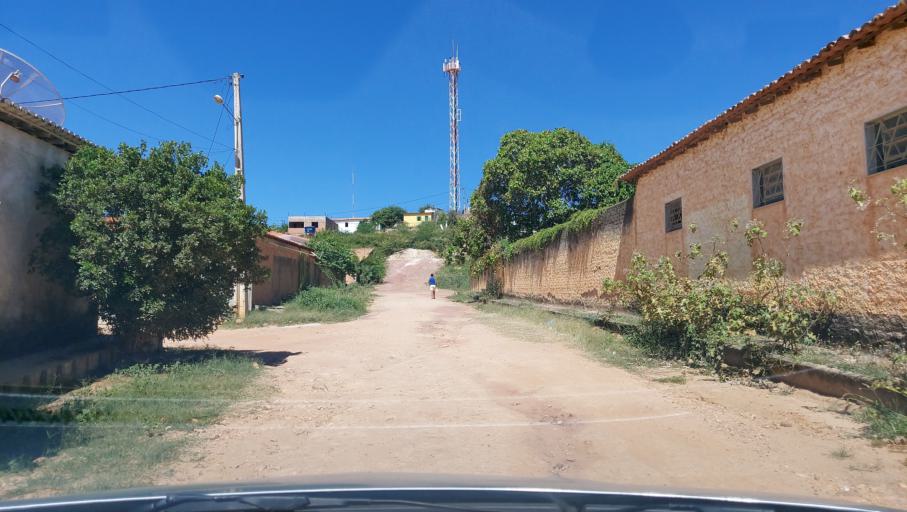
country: BR
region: Bahia
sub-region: Oliveira Dos Brejinhos
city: Beira Rio
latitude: -12.0044
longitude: -42.6265
